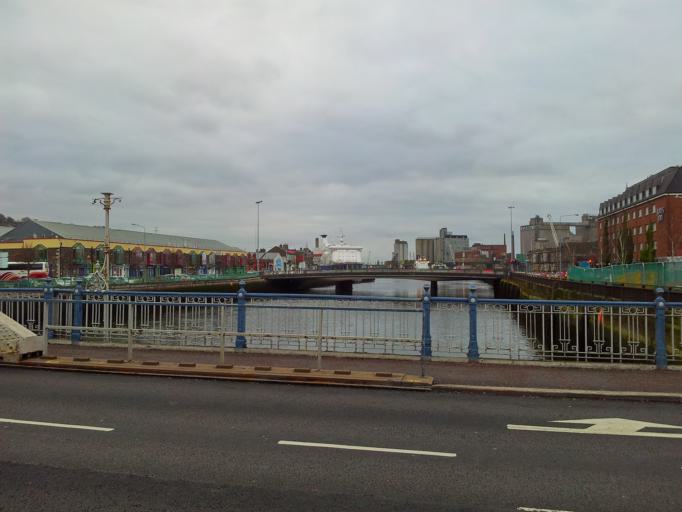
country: IE
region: Munster
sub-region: County Cork
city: Cork
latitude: 51.9004
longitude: -8.4704
